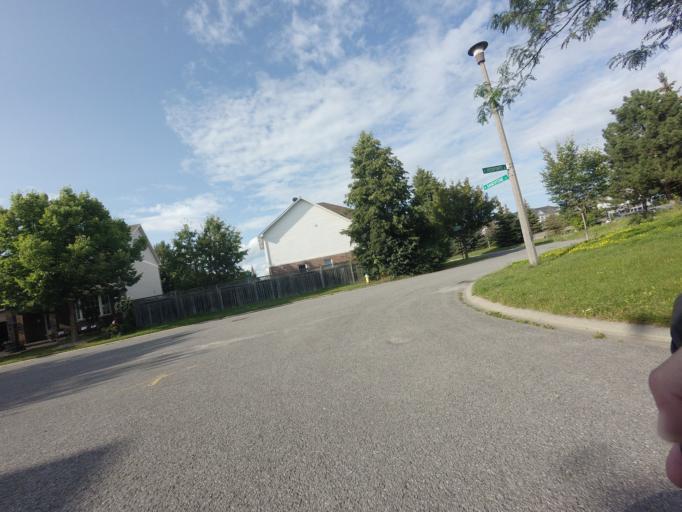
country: CA
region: Ontario
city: Bells Corners
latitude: 45.2773
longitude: -75.7162
